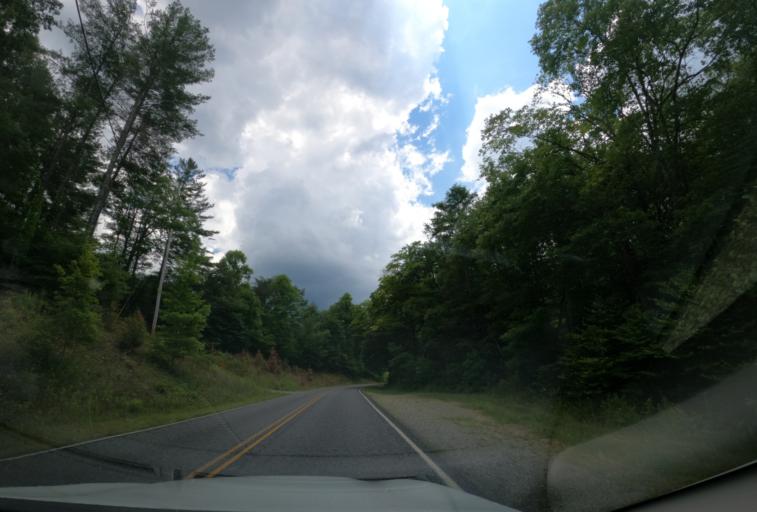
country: US
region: North Carolina
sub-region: Haywood County
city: Hazelwood
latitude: 35.4034
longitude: -82.8985
